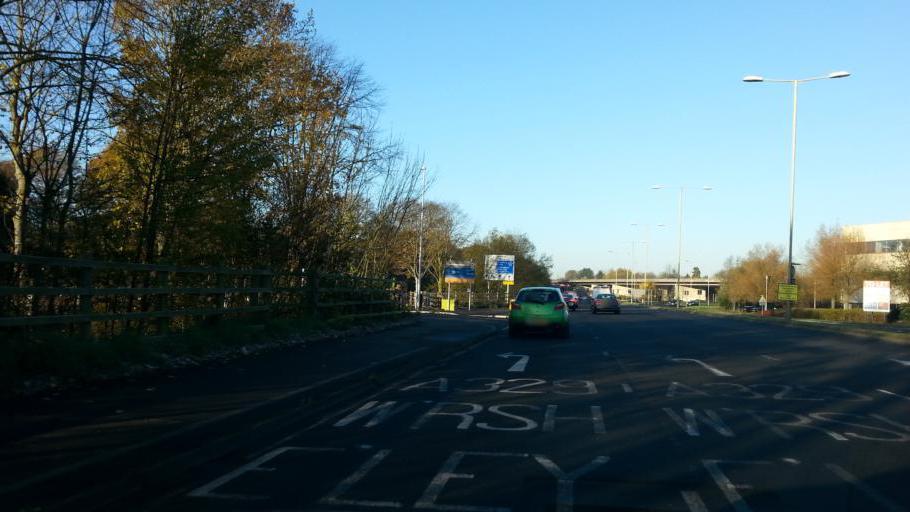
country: GB
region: England
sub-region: Wokingham
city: Woodley
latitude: 51.4379
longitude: -0.8929
